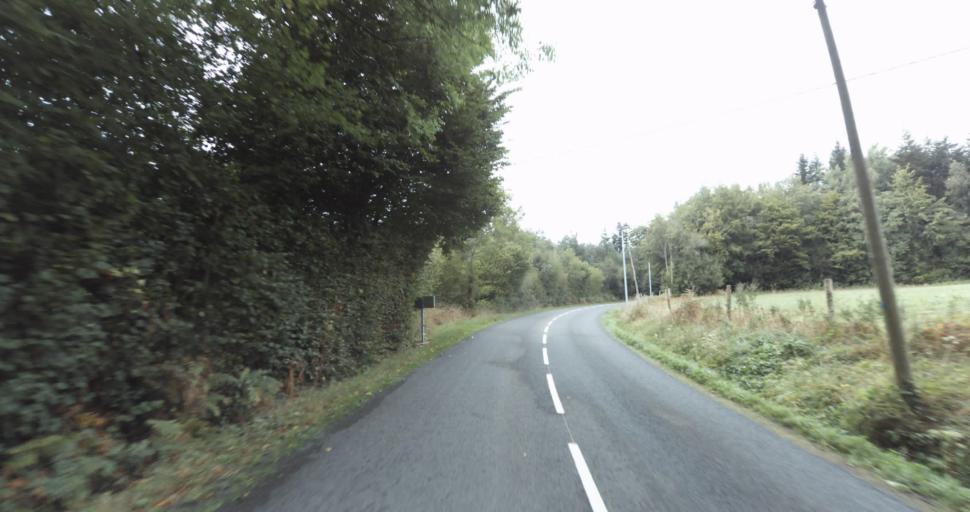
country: FR
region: Lower Normandy
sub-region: Departement de l'Orne
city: Sainte-Gauburge-Sainte-Colombe
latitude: 48.7501
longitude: 0.4359
